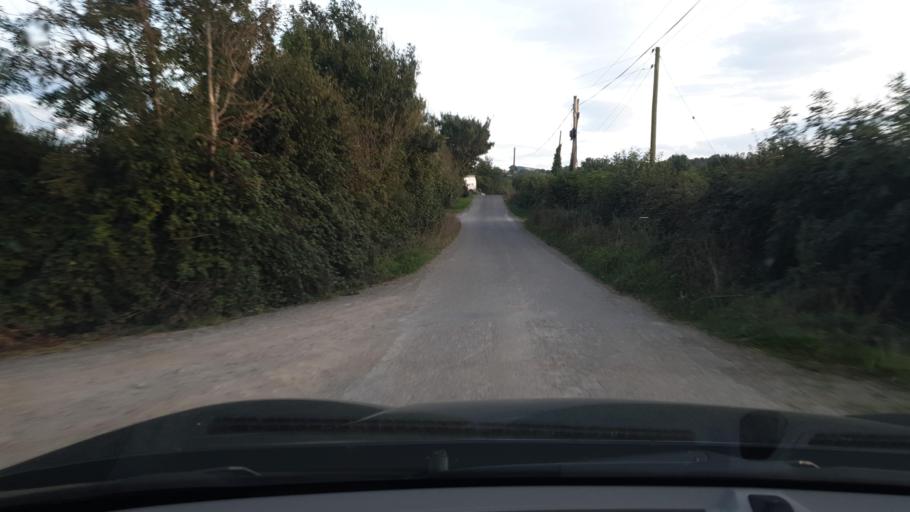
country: IE
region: Leinster
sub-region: An Mhi
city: Stamullin
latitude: 53.5816
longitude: -6.2456
